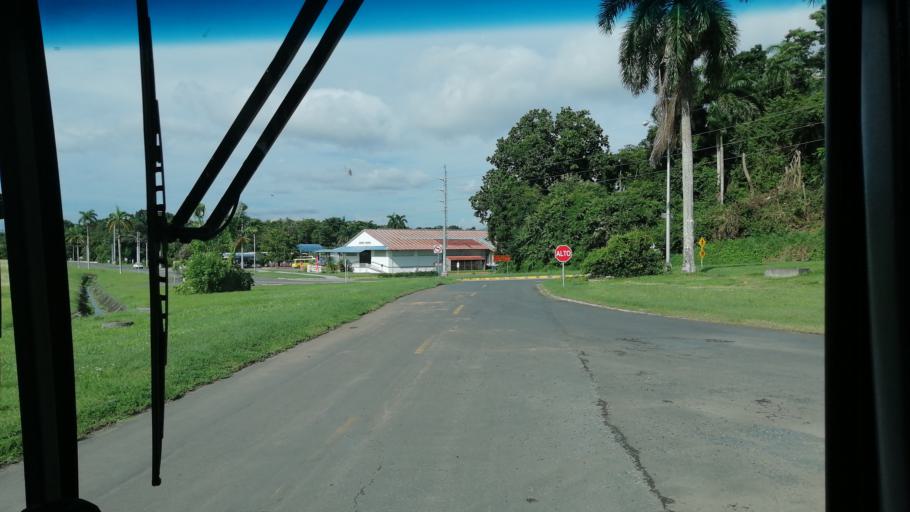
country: PA
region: Panama
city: Veracruz
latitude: 8.9196
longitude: -79.5923
